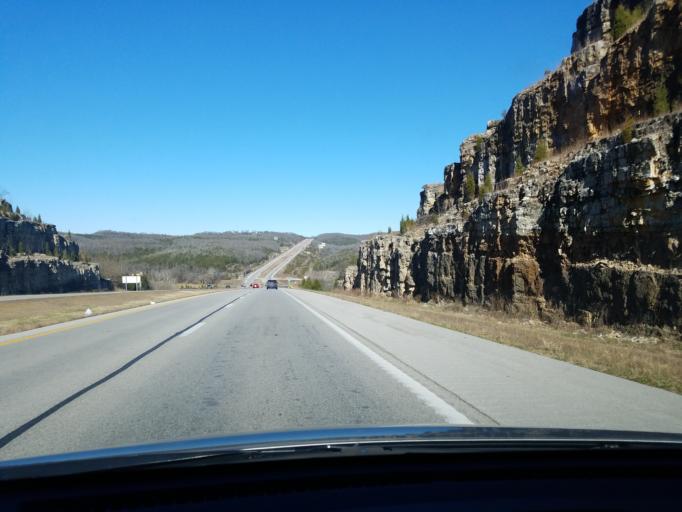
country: US
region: Missouri
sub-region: Taney County
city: Merriam Woods
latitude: 36.7631
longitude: -93.2229
